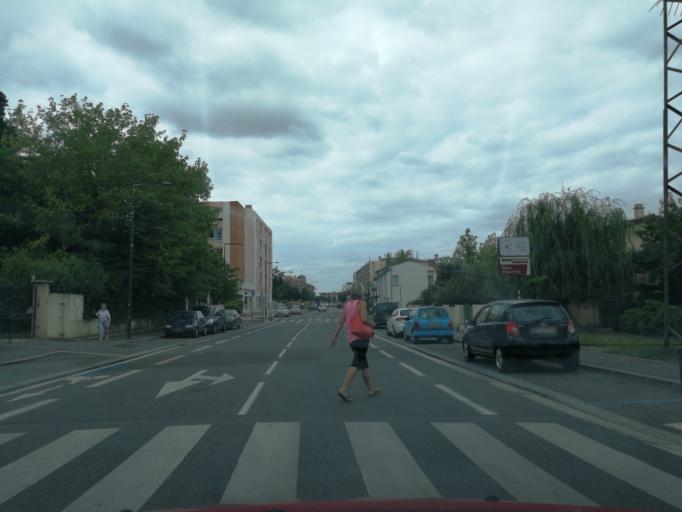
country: FR
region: Midi-Pyrenees
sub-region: Departement de la Haute-Garonne
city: Ramonville-Saint-Agne
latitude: 43.5500
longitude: 1.4707
